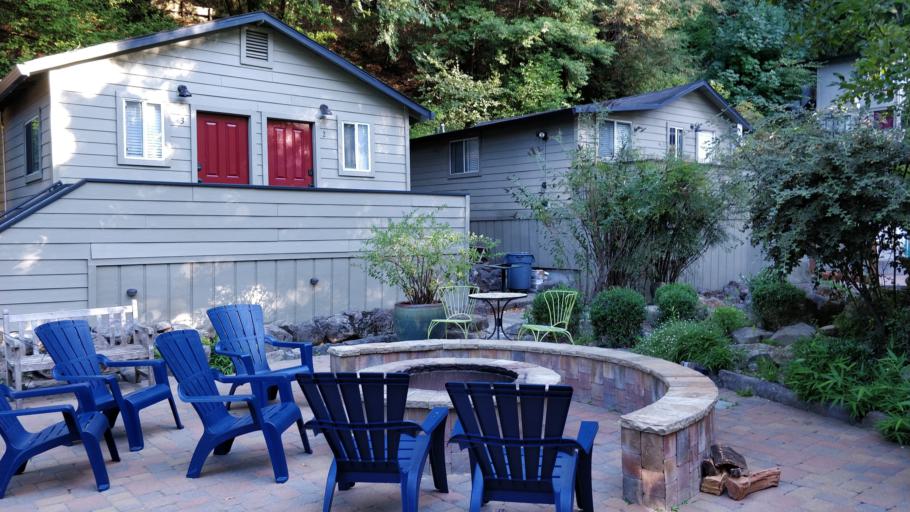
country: US
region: California
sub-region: Sonoma County
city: Guerneville
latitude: 38.5157
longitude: -122.9833
